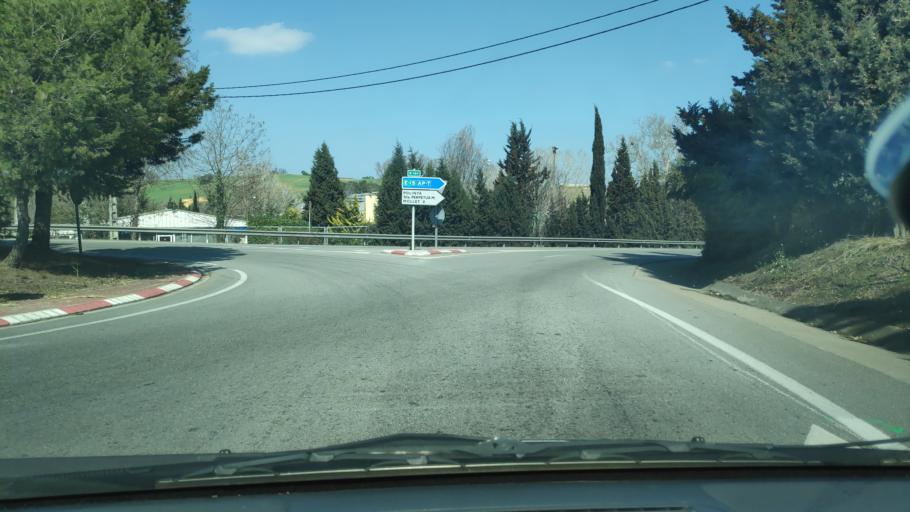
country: ES
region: Catalonia
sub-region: Provincia de Barcelona
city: Polinya
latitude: 41.5330
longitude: 2.1536
